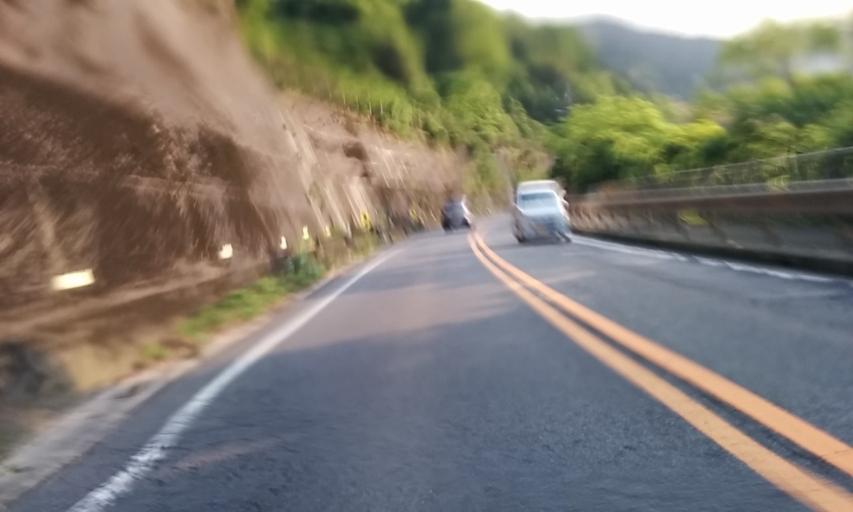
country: JP
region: Ehime
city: Saijo
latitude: 33.8531
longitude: 133.0111
